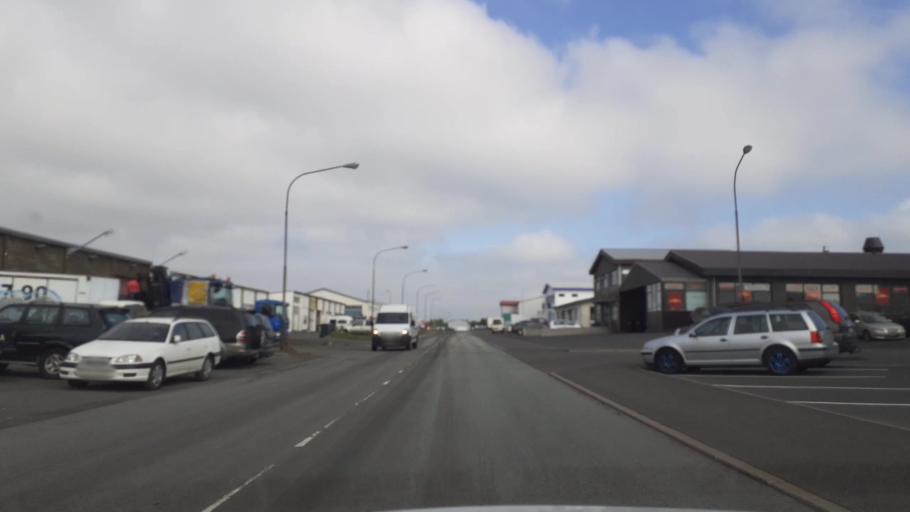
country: IS
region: Capital Region
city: Hafnarfjoerdur
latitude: 64.0778
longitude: -21.9357
